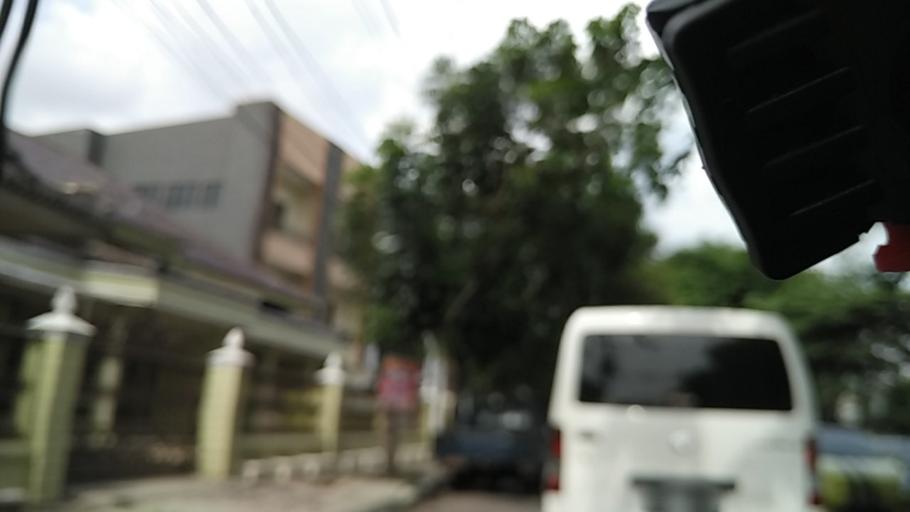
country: ID
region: Central Java
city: Semarang
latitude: -7.0010
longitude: 110.4248
